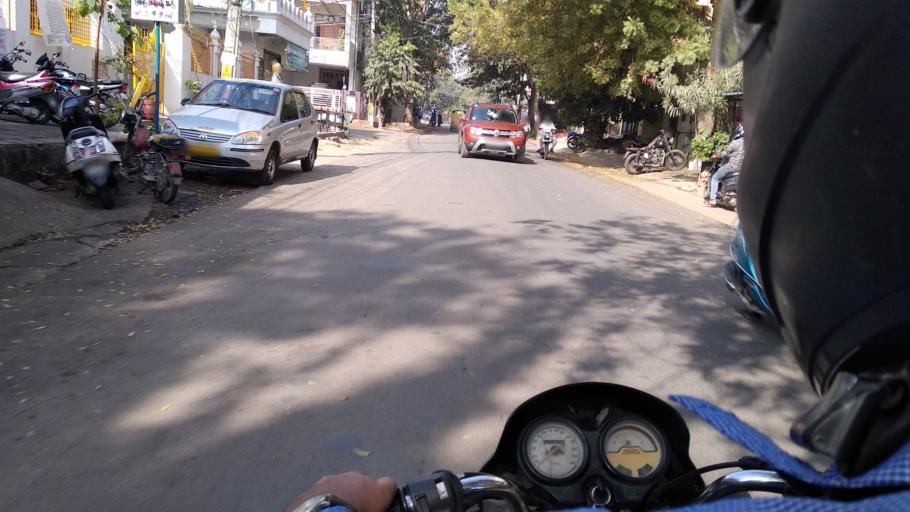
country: IN
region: Telangana
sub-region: Rangareddi
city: Lal Bahadur Nagar
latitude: 17.3329
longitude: 78.5720
